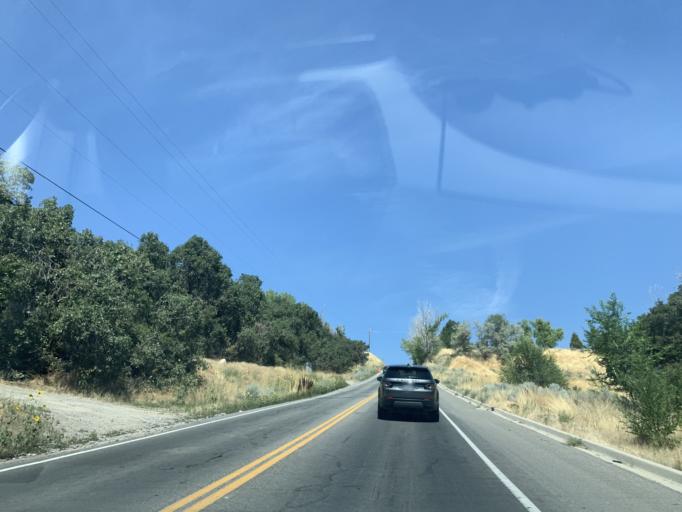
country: US
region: Utah
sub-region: Utah County
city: Lehi
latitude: 40.4230
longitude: -111.8305
